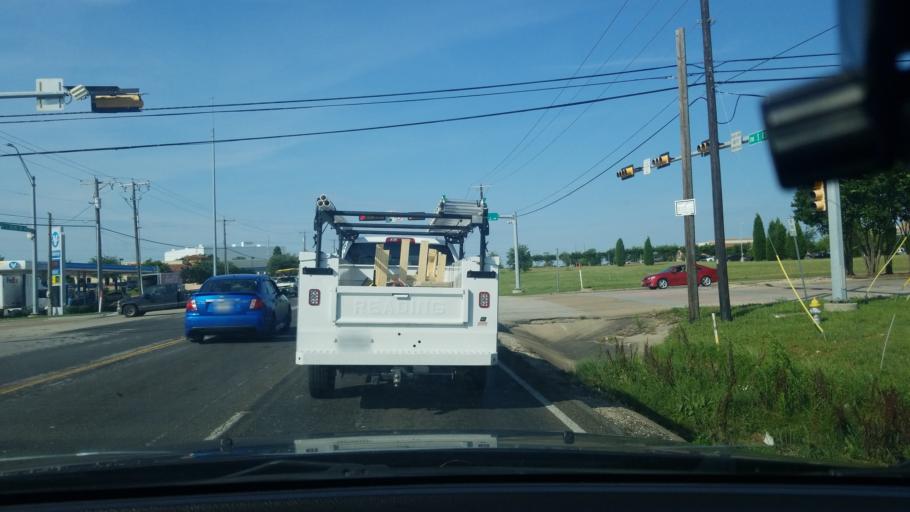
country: US
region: Texas
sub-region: Dallas County
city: Sunnyvale
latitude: 32.7798
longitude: -96.5661
